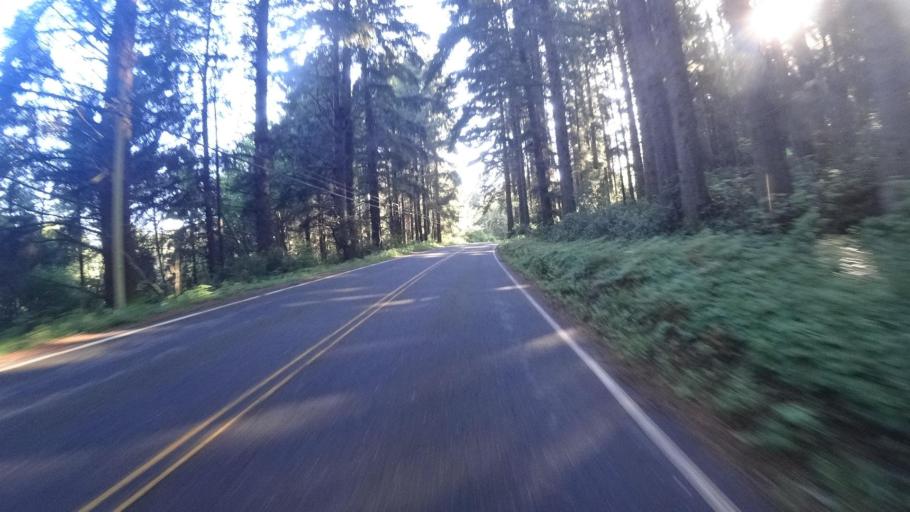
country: US
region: California
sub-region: Humboldt County
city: Westhaven-Moonstone
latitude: 41.1348
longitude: -124.1520
